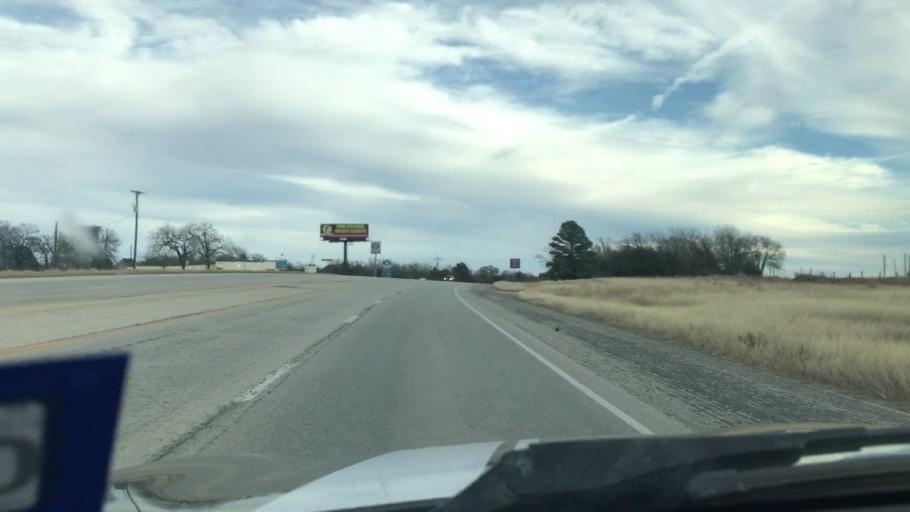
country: US
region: Texas
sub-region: Bastrop County
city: Camp Swift
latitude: 30.2946
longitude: -97.2602
